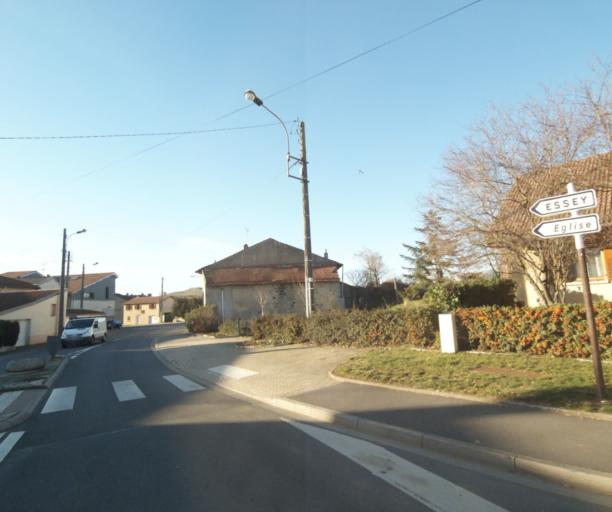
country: FR
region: Lorraine
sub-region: Departement de Meurthe-et-Moselle
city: Seichamps
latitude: 48.7154
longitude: 6.2690
